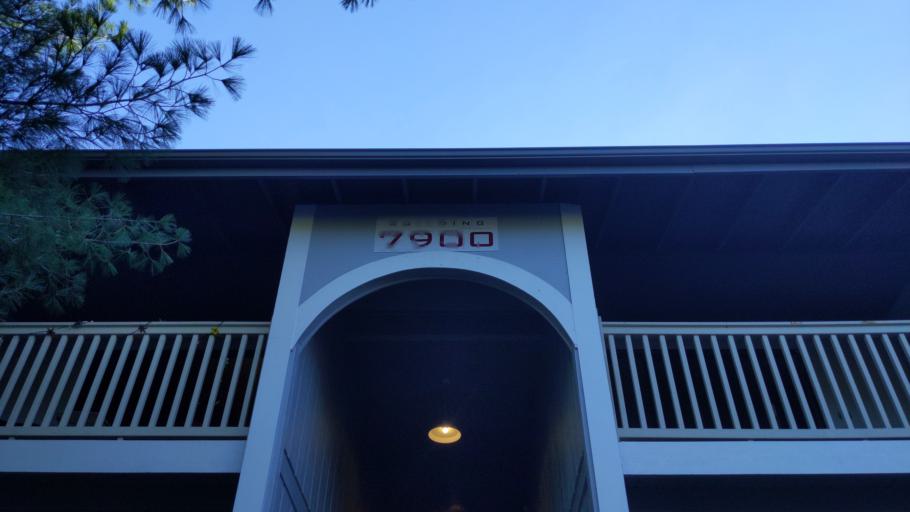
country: US
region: Virginia
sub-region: Montgomery County
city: Blacksburg
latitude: 37.2424
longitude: -80.4216
